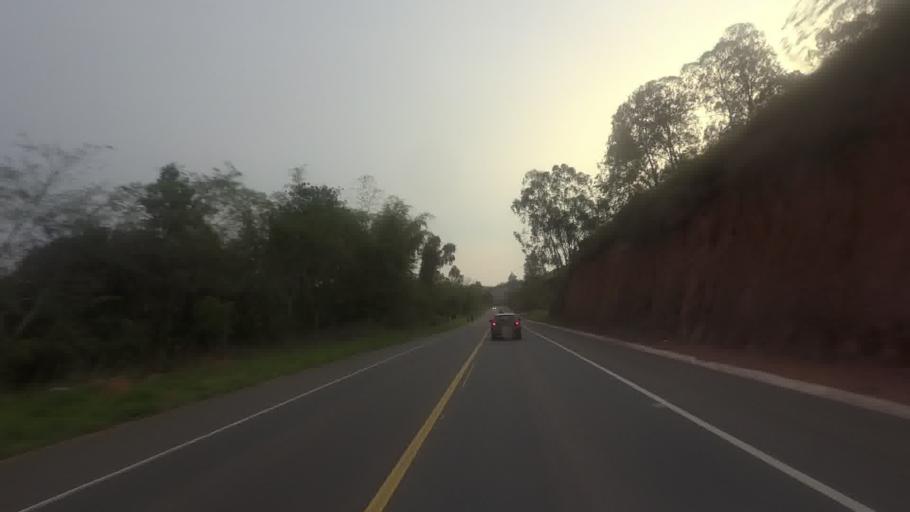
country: BR
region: Rio de Janeiro
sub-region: Carmo
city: Carmo
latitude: -21.7834
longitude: -42.5454
